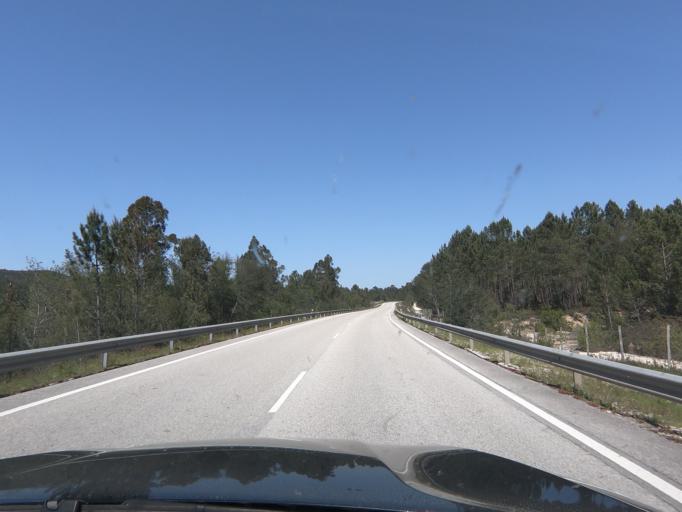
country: PT
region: Coimbra
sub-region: Miranda do Corvo
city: Miranda do Corvo
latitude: 40.1010
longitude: -8.3083
